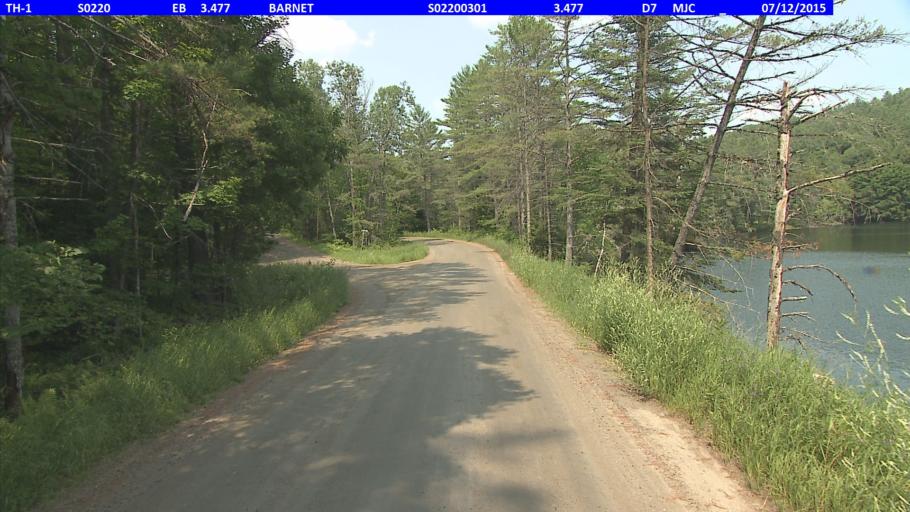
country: US
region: Vermont
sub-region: Caledonia County
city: Saint Johnsbury
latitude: 44.3421
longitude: -71.9943
